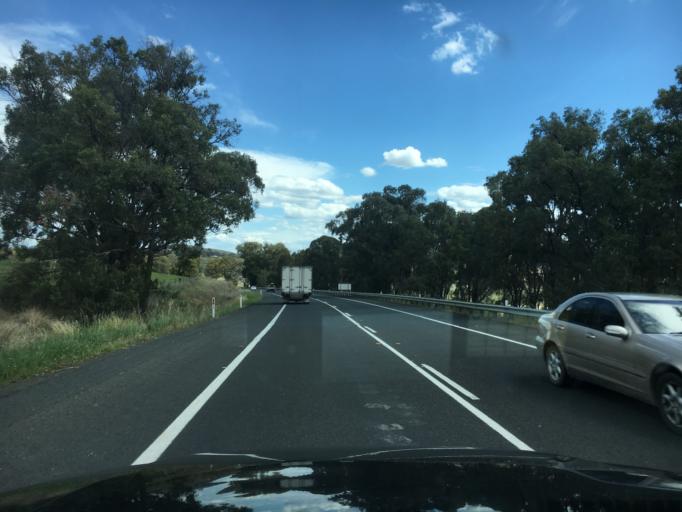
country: AU
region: New South Wales
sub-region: Liverpool Plains
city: Quirindi
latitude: -31.4687
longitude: 150.8602
